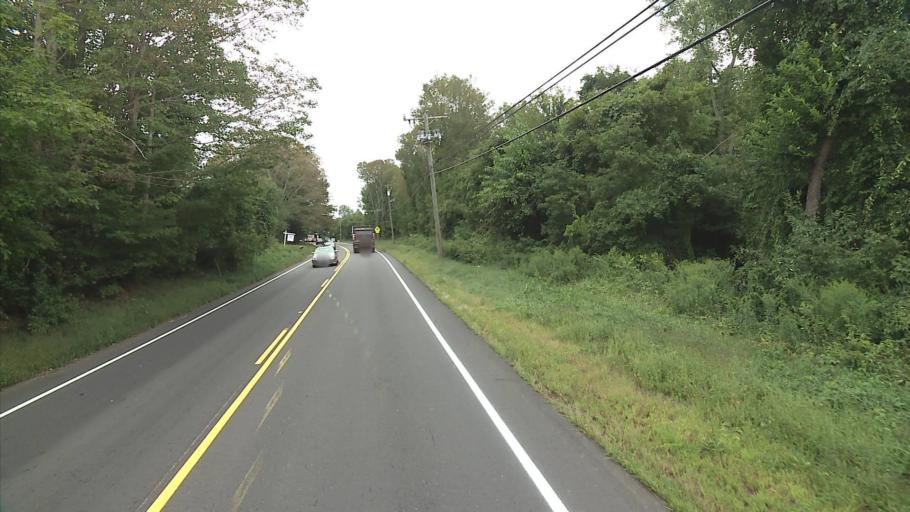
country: US
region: Connecticut
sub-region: Tolland County
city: Hebron
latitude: 41.6493
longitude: -72.3595
